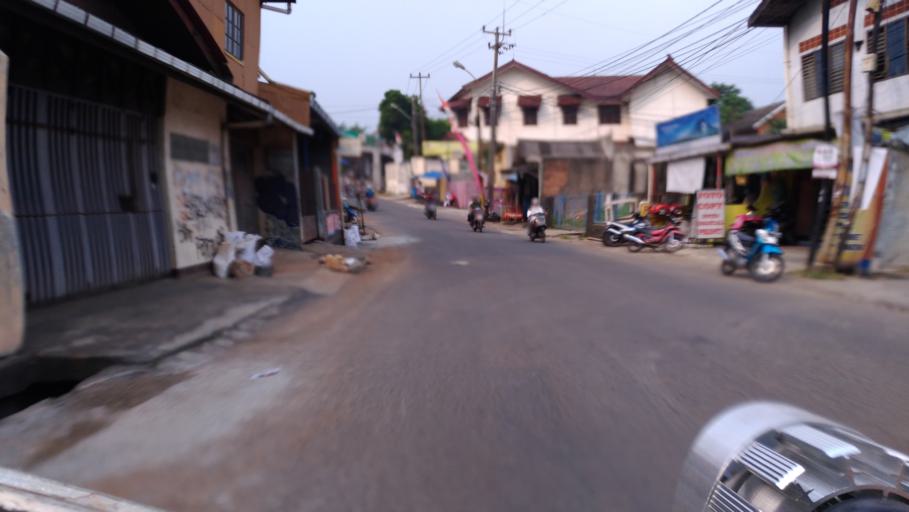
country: ID
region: West Java
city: Depok
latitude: -6.3657
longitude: 106.8614
